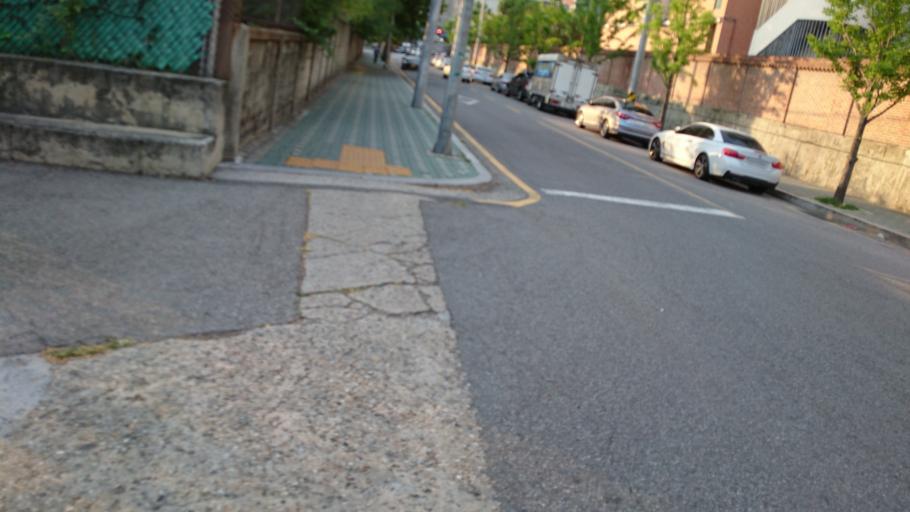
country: KR
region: Seoul
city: Seoul
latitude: 37.5448
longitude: 126.9789
